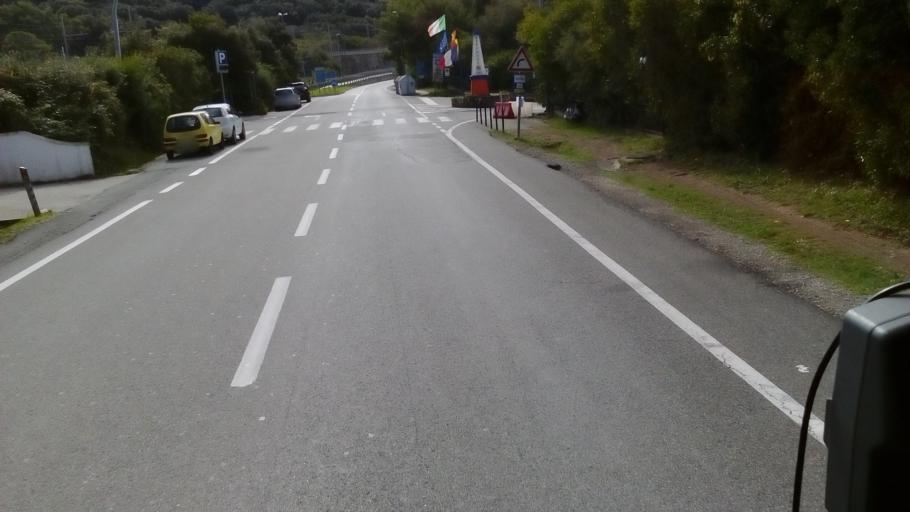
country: IT
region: Tuscany
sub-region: Provincia di Livorno
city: Quercianella
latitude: 43.4817
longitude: 10.3333
